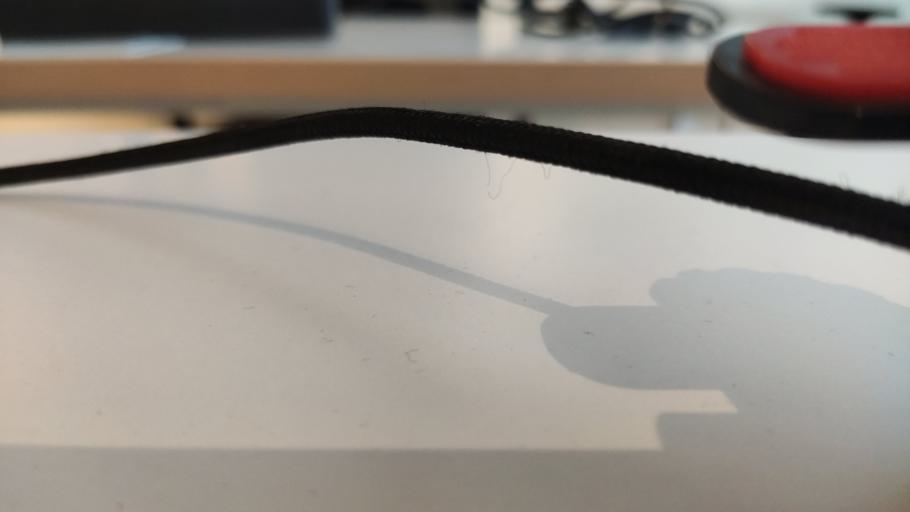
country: RU
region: Moskovskaya
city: Novopetrovskoye
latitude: 55.9790
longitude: 36.4493
